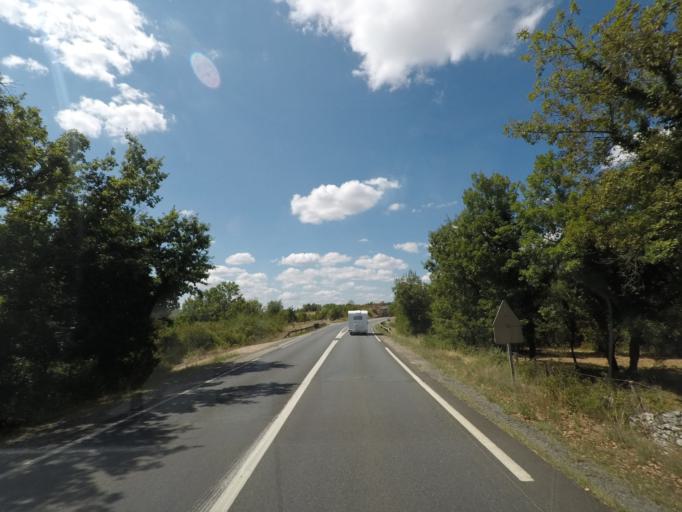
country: FR
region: Midi-Pyrenees
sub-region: Departement du Lot
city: Lacapelle-Marival
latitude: 44.6271
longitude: 1.8827
